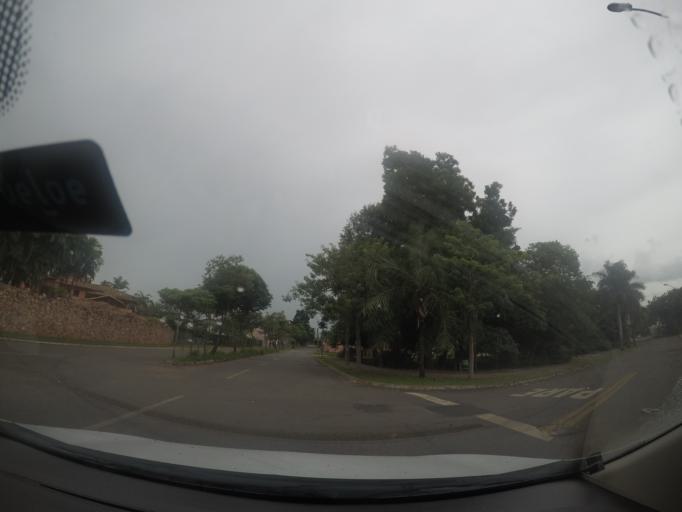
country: BR
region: Goias
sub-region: Goiania
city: Goiania
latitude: -16.6482
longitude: -49.2346
